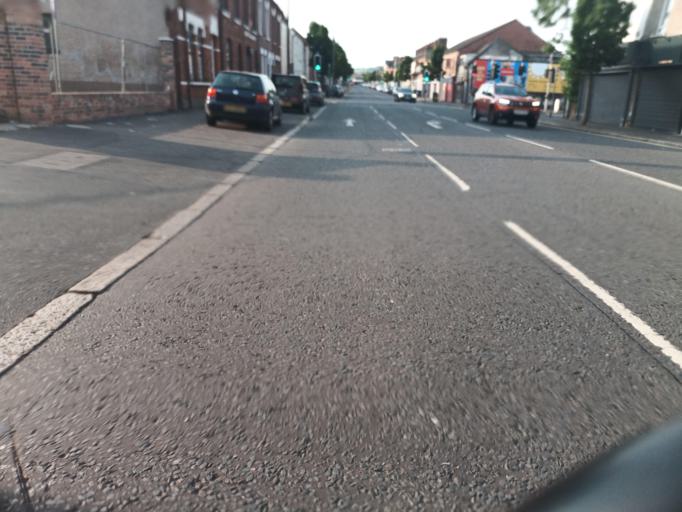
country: GB
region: Northern Ireland
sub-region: Castlereagh District
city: Castlereagh
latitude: 54.5974
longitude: -5.8896
